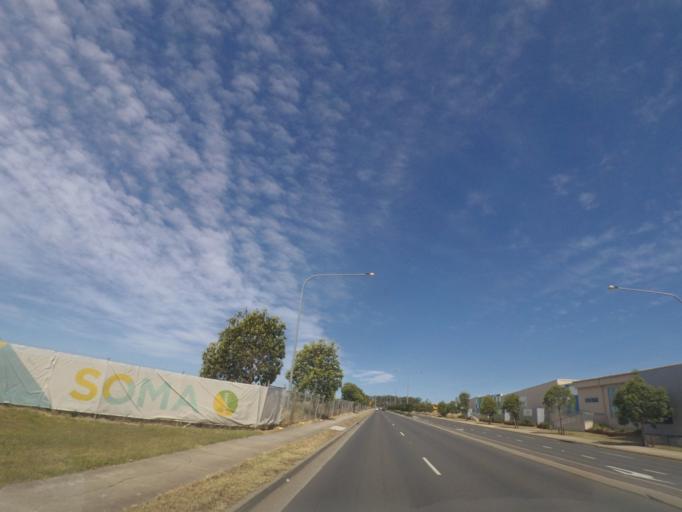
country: AU
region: New South Wales
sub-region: Camden
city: Narellan
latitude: -34.0224
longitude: 150.7664
